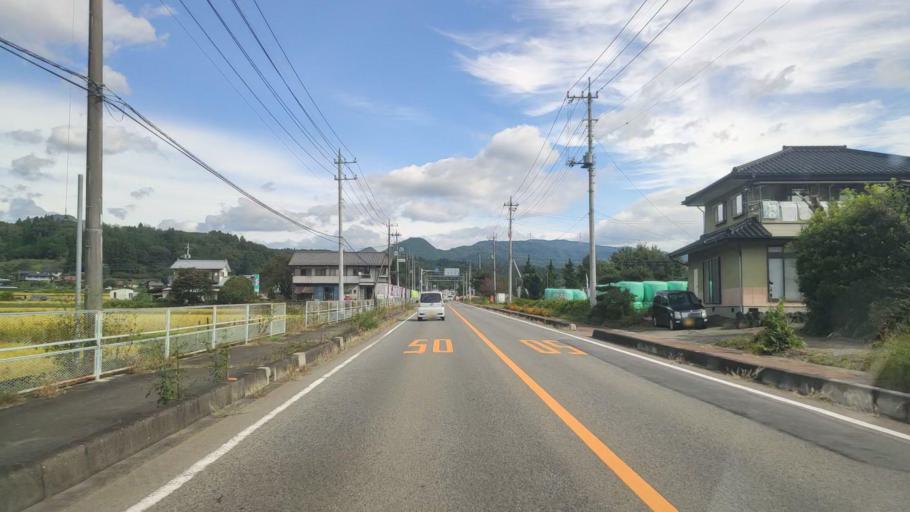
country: JP
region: Gunma
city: Nakanojomachi
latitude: 36.5948
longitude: 138.8622
